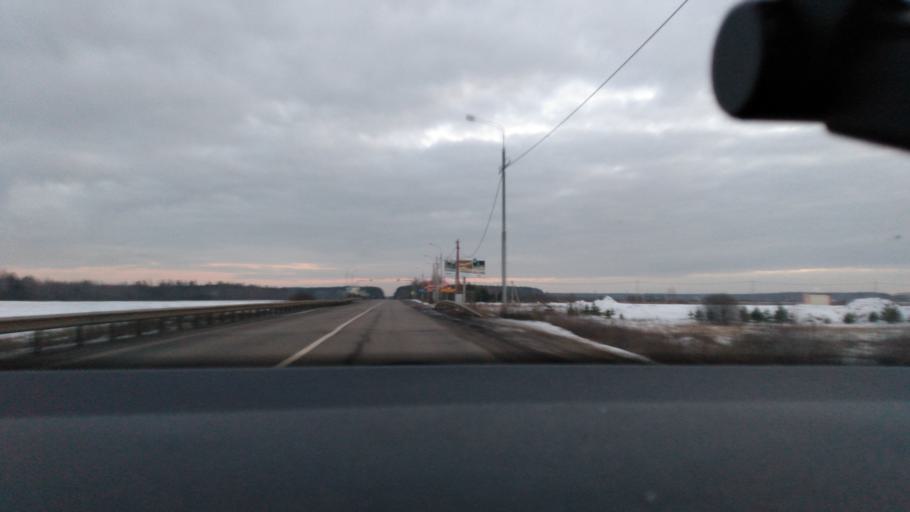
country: RU
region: Moskovskaya
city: Yegor'yevsk
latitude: 55.4408
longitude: 39.0191
